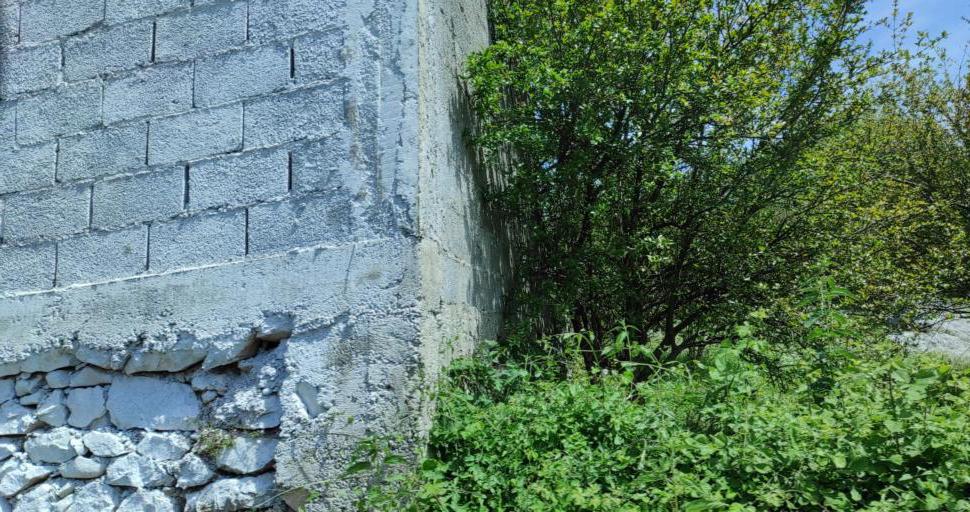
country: AL
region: Shkoder
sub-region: Rrethi i Malesia e Madhe
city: Gruemire
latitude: 42.1434
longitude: 19.5468
